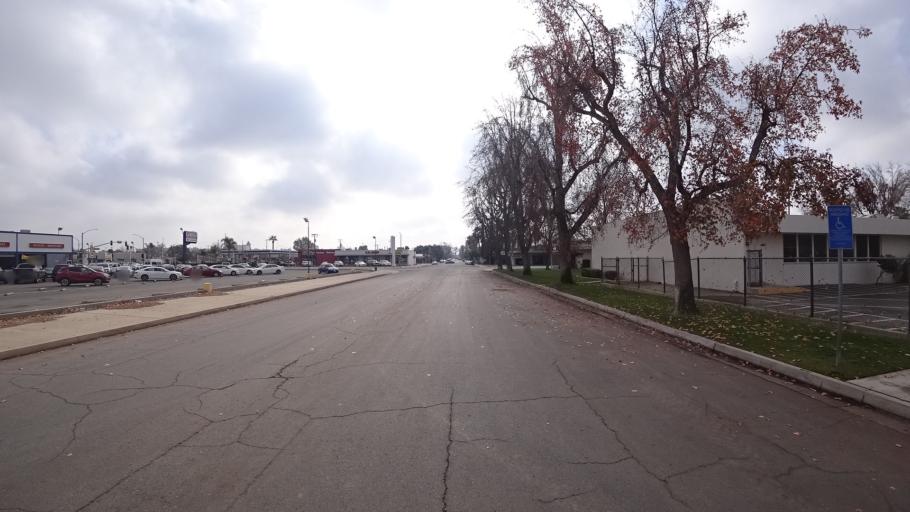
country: US
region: California
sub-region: Kern County
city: Bakersfield
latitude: 35.3818
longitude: -119.0247
